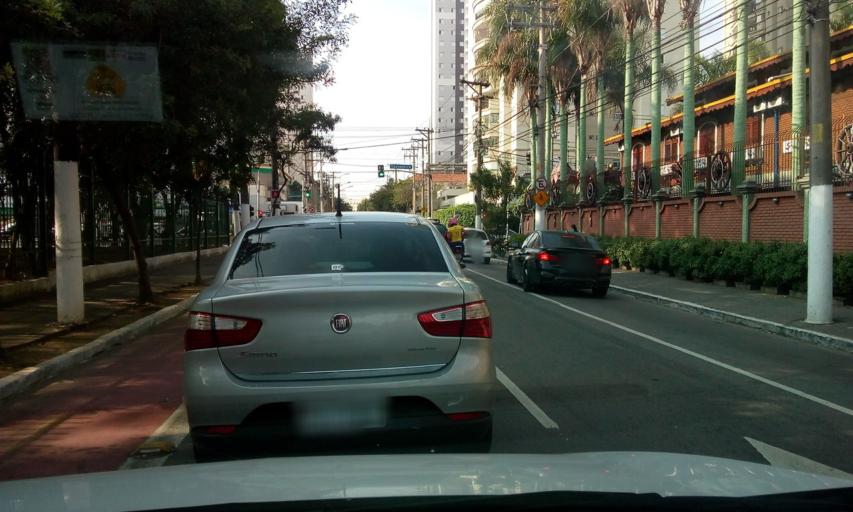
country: BR
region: Sao Paulo
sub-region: Sao Paulo
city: Sao Paulo
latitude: -23.5500
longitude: -46.5965
